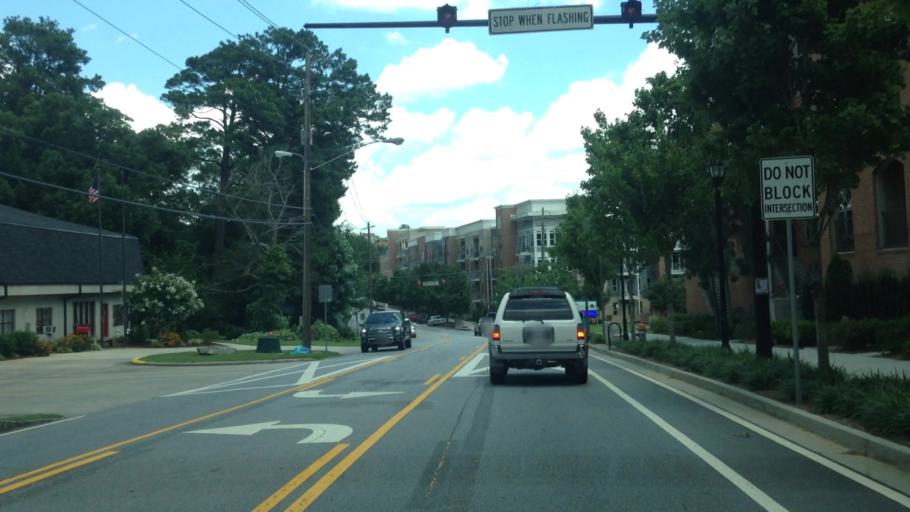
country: US
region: Georgia
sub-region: DeKalb County
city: North Atlanta
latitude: 33.8604
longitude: -84.3357
